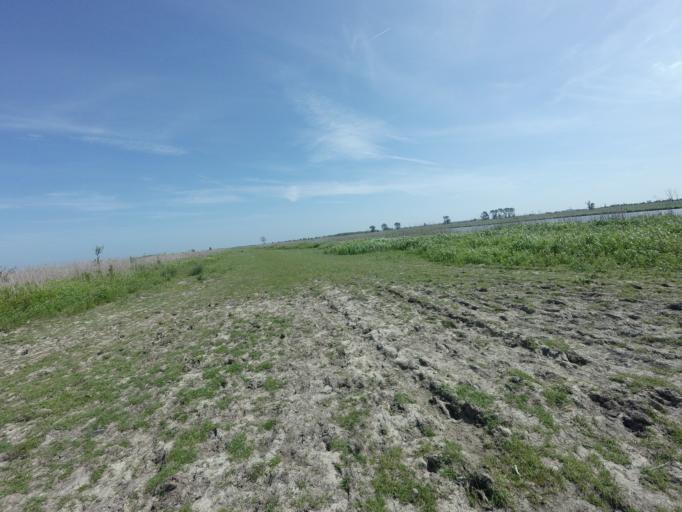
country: NL
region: South Holland
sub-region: Gemeente Spijkenisse
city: Spijkenisse
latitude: 51.7387
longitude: 4.3097
